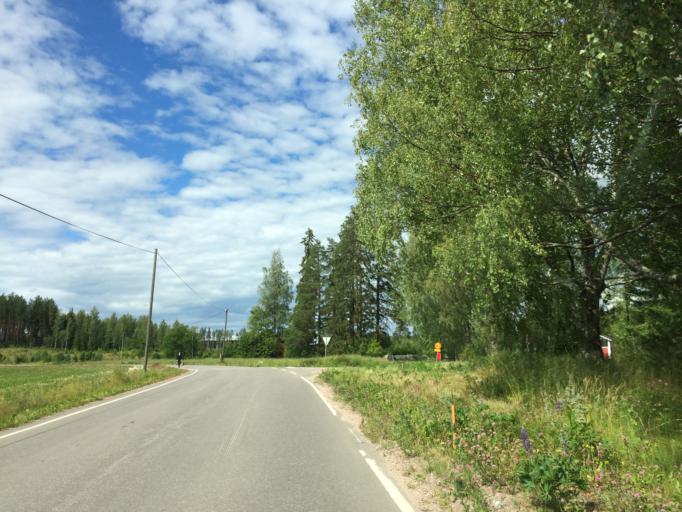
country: FI
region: Haeme
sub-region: Haemeenlinna
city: Tervakoski
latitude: 60.8405
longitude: 24.5604
